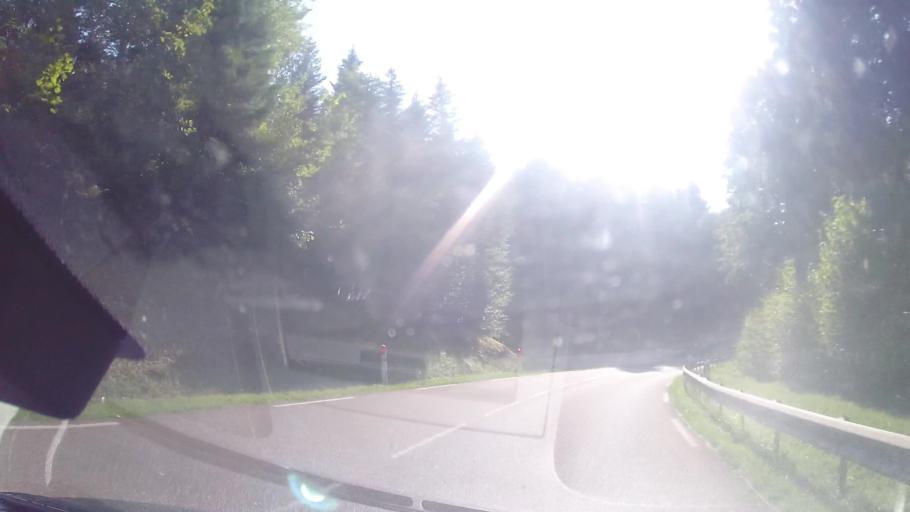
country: FR
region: Franche-Comte
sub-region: Departement du Jura
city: Clairvaux-les-Lacs
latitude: 46.5847
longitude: 5.8326
